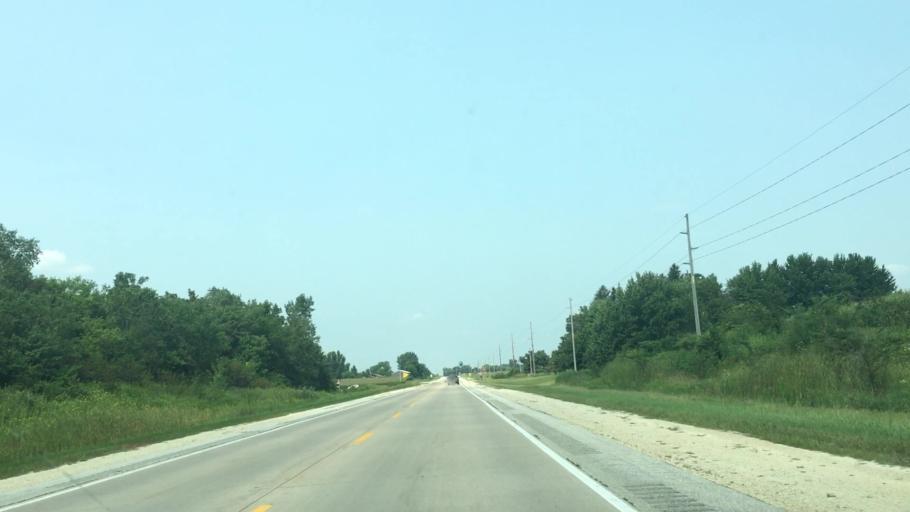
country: US
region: Iowa
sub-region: Fayette County
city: Oelwein
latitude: 42.6007
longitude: -91.9023
